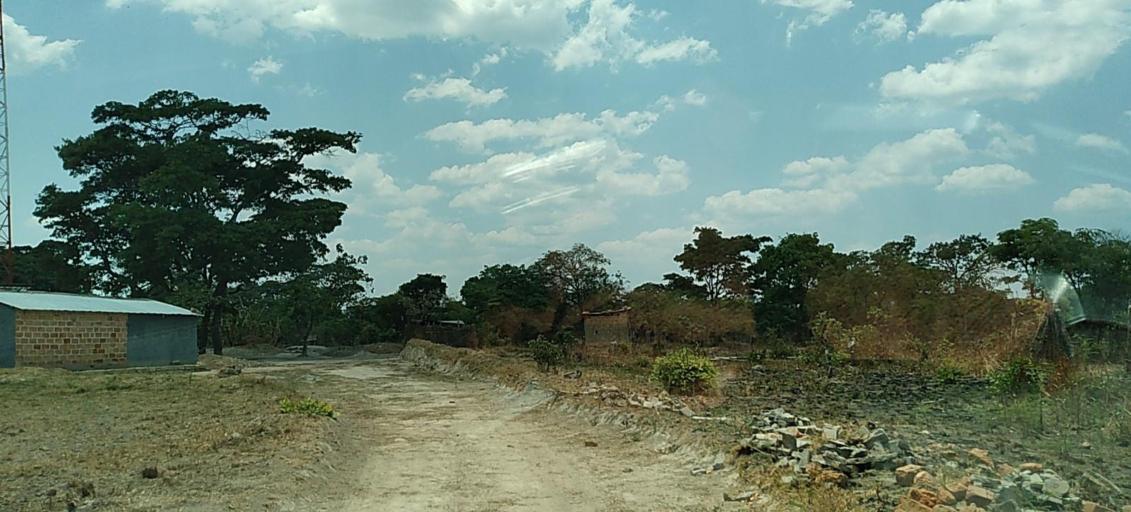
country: ZM
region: Copperbelt
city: Chililabombwe
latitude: -12.4493
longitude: 27.6802
